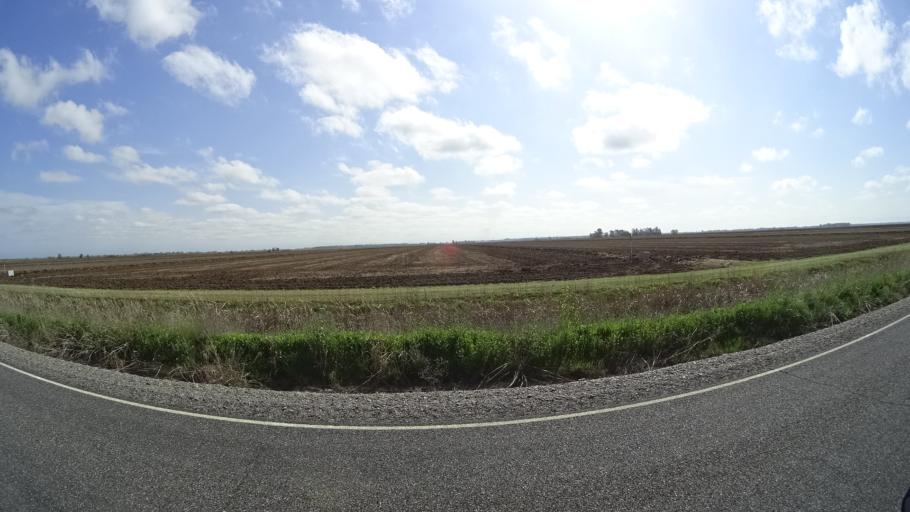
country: US
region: California
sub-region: Butte County
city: Durham
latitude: 39.5101
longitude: -121.9299
